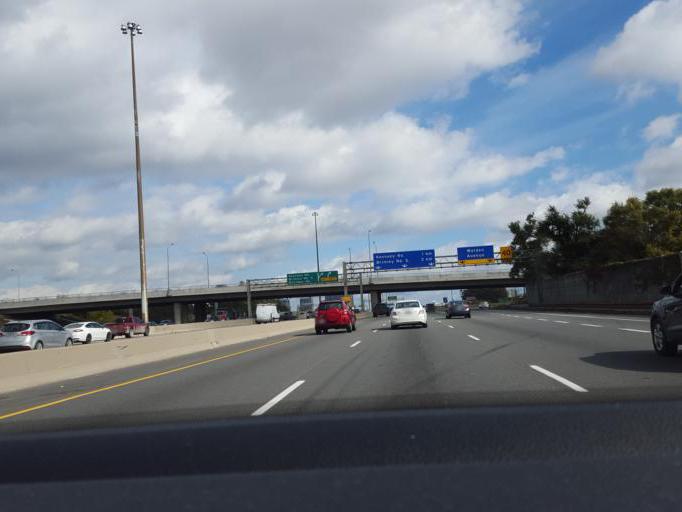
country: CA
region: Ontario
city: Scarborough
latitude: 43.7697
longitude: -79.3058
